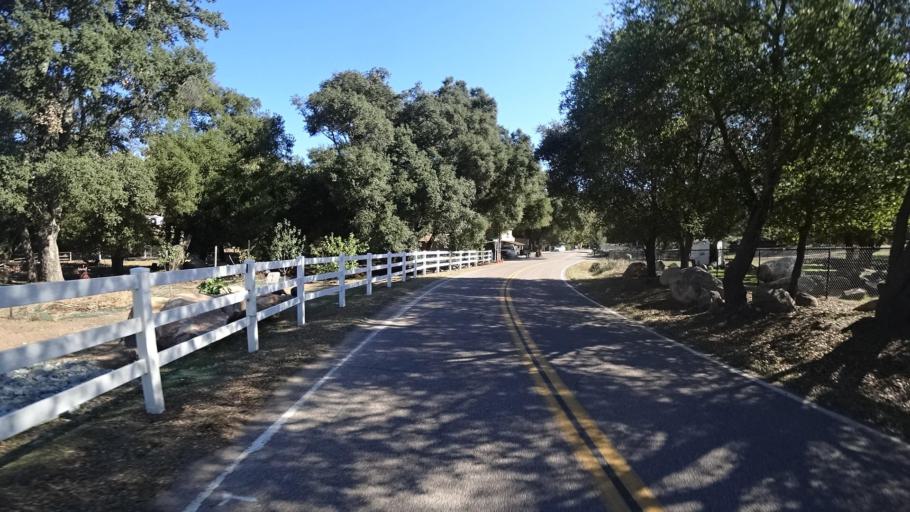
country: US
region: California
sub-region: San Diego County
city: Jamul
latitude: 32.7157
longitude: -116.7693
